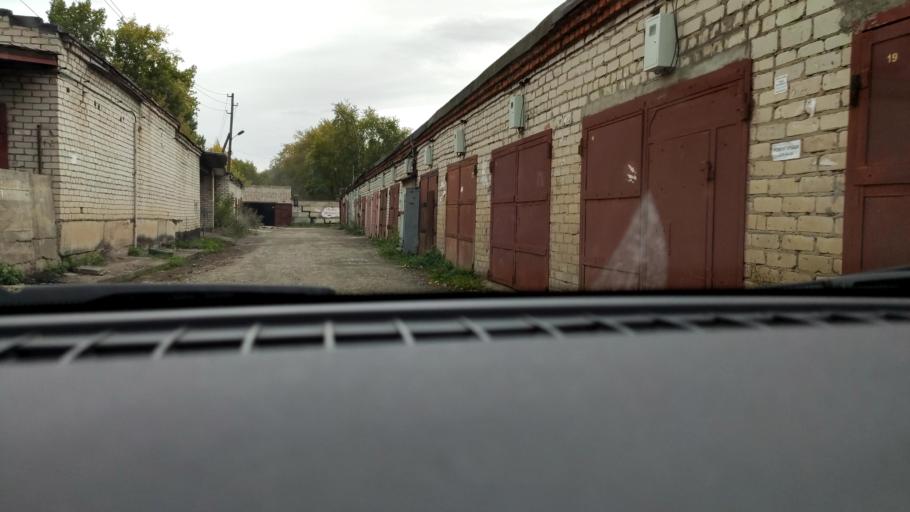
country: RU
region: Perm
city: Perm
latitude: 57.9763
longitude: 56.2202
